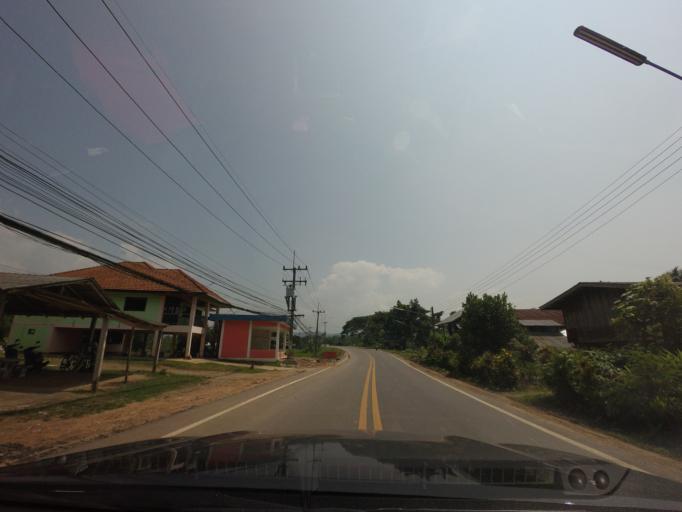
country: TH
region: Nan
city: Santi Suk
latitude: 18.9235
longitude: 100.9248
